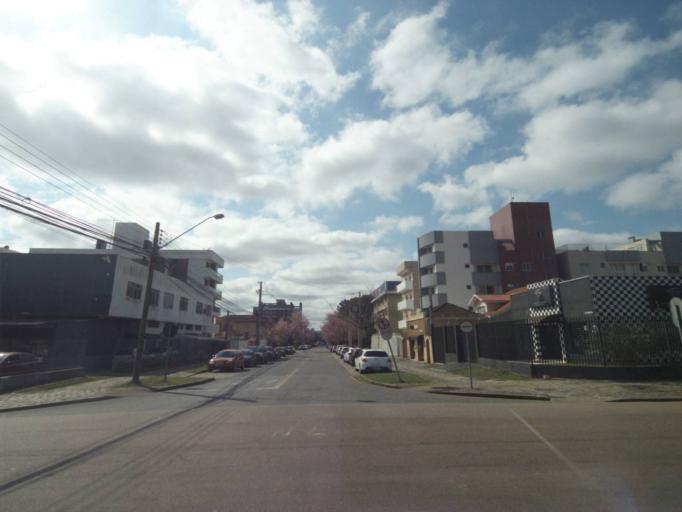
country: BR
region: Parana
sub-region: Curitiba
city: Curitiba
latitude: -25.4494
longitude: -49.2674
